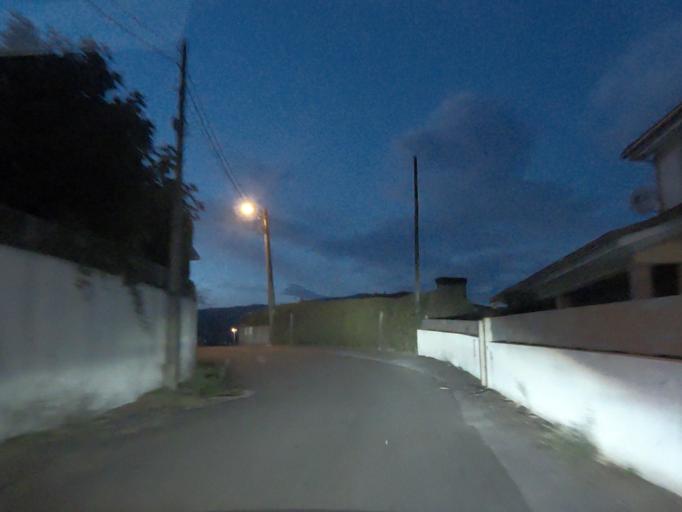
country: PT
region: Vila Real
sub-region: Vila Real
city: Vila Real
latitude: 41.2803
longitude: -7.7578
